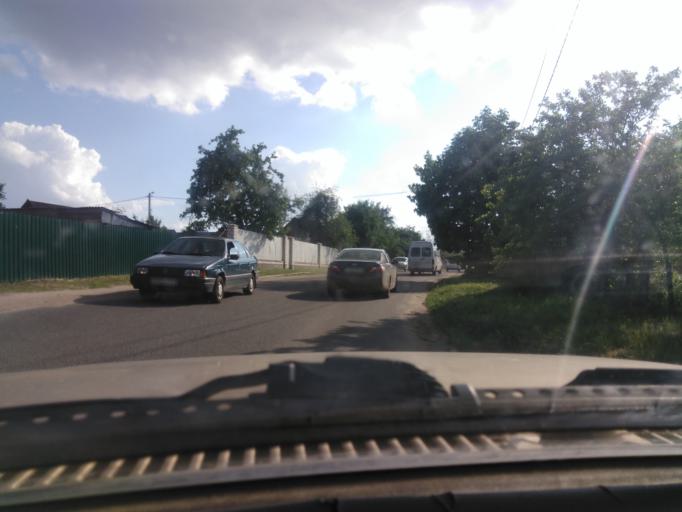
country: BY
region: Mogilev
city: Mahilyow
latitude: 53.9306
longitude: 30.3213
